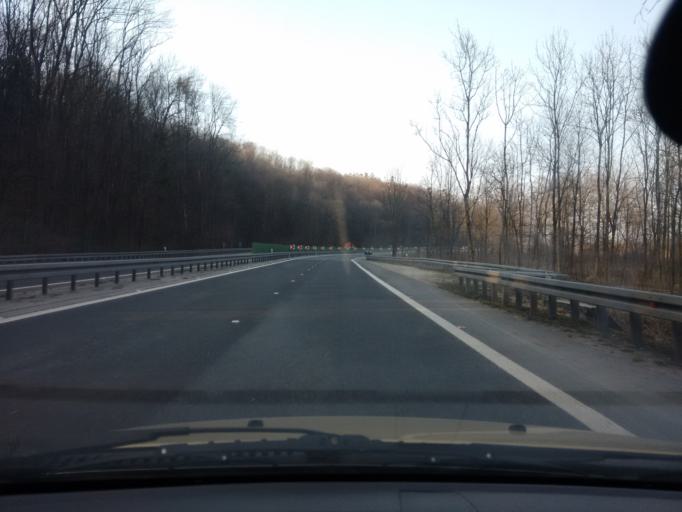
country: PL
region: Silesian Voivodeship
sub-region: Powiat cieszynski
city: Skoczow
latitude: 49.8166
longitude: 18.7915
